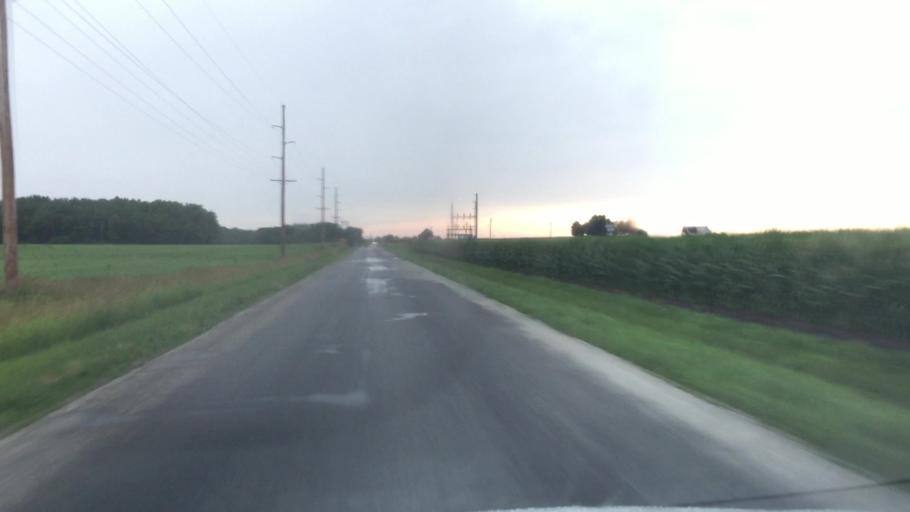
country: US
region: Iowa
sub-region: Lee County
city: Fort Madison
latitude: 40.5625
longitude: -91.2686
